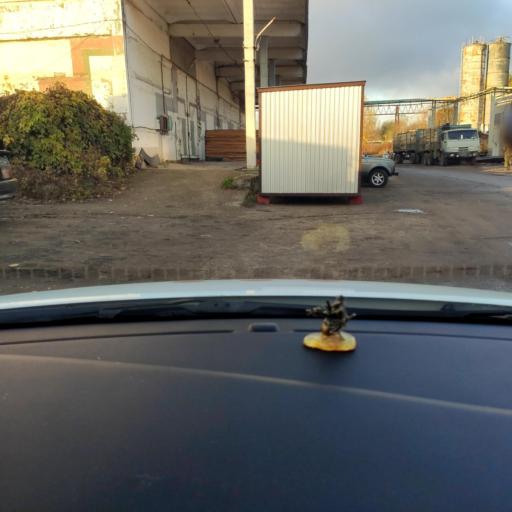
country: RU
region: Tatarstan
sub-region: Gorod Kazan'
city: Kazan
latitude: 55.7777
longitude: 49.1827
